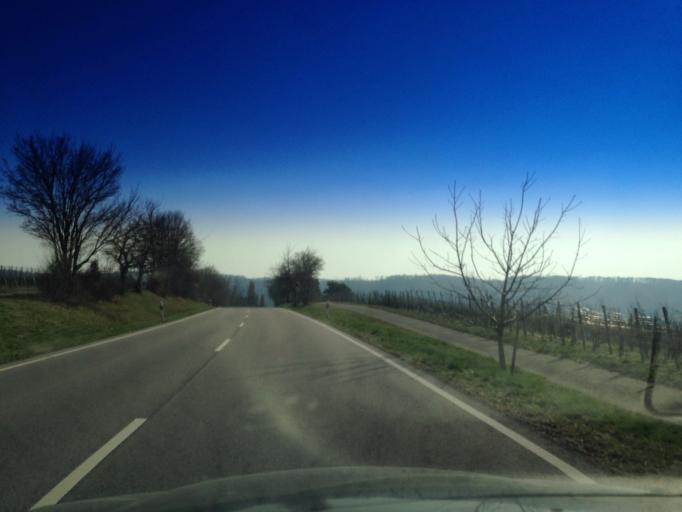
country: DE
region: Baden-Wuerttemberg
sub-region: Karlsruhe Region
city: Illingen
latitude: 48.9408
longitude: 8.9081
